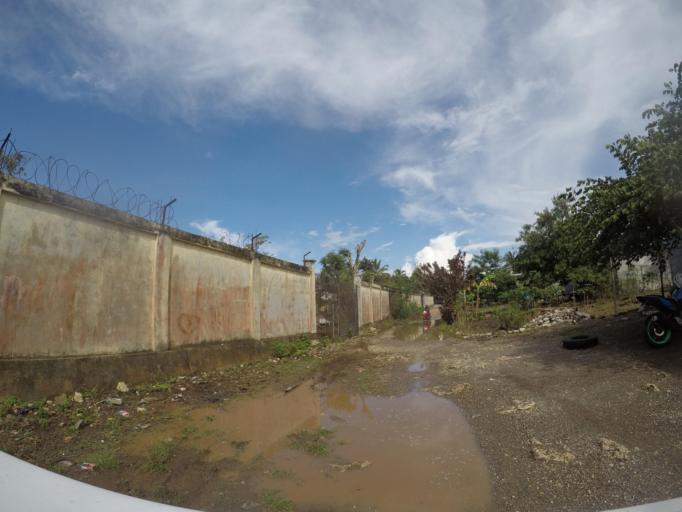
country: TL
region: Baucau
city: Baucau
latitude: -8.4802
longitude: 126.4564
